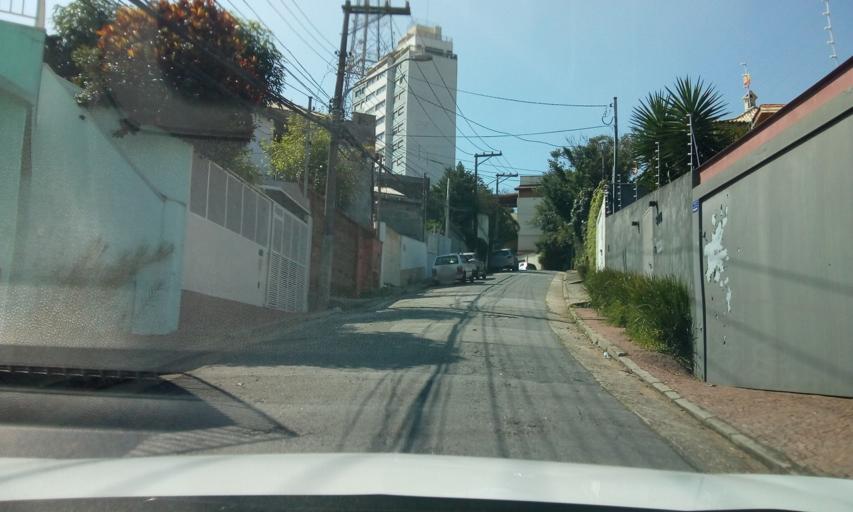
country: BR
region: Sao Paulo
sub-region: Sao Paulo
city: Sao Paulo
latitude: -23.5443
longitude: -46.6843
